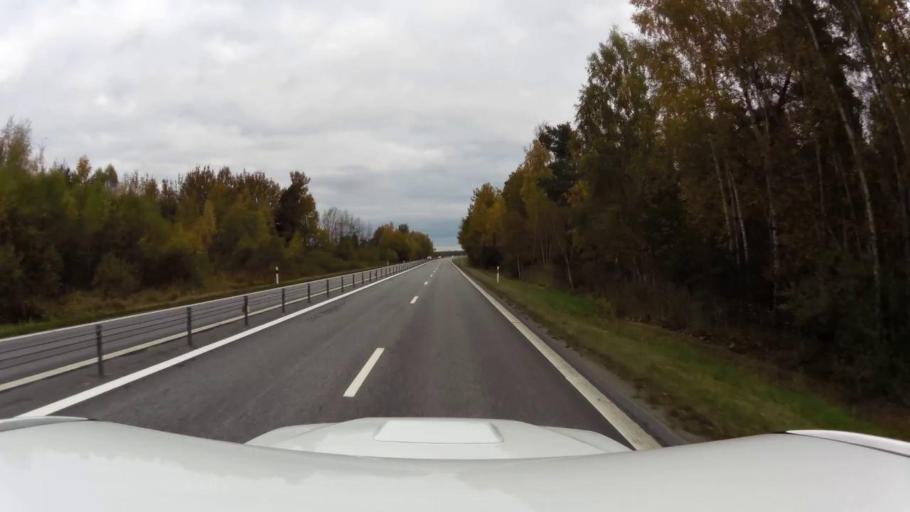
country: SE
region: OEstergoetland
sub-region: Linkopings Kommun
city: Malmslatt
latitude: 58.4423
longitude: 15.5192
